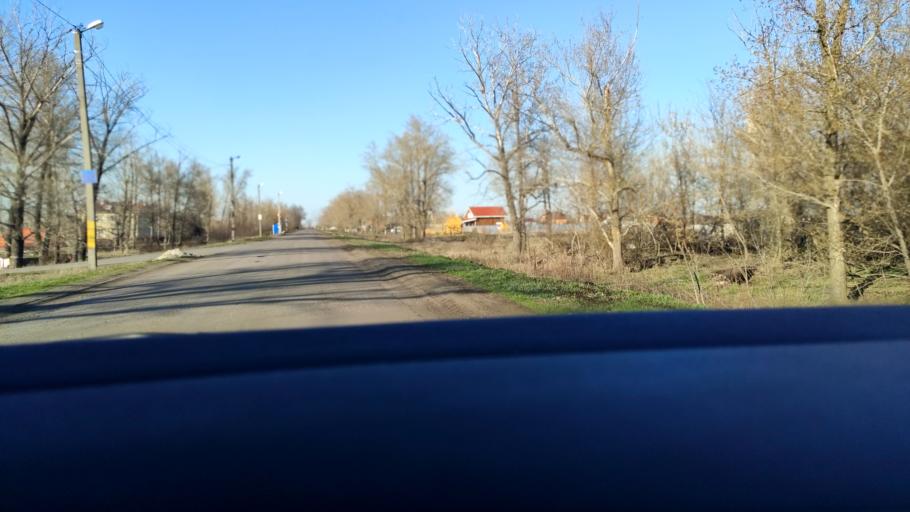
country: RU
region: Voronezj
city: Maslovka
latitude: 51.5102
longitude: 39.2947
